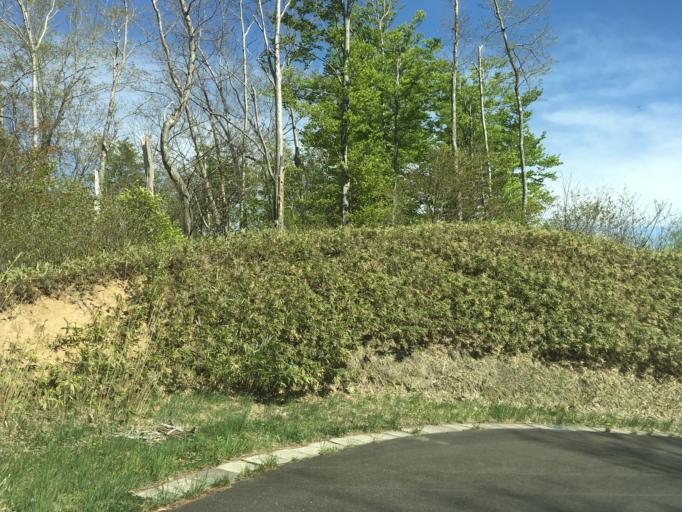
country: JP
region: Iwate
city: Mizusawa
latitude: 39.1169
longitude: 140.9212
